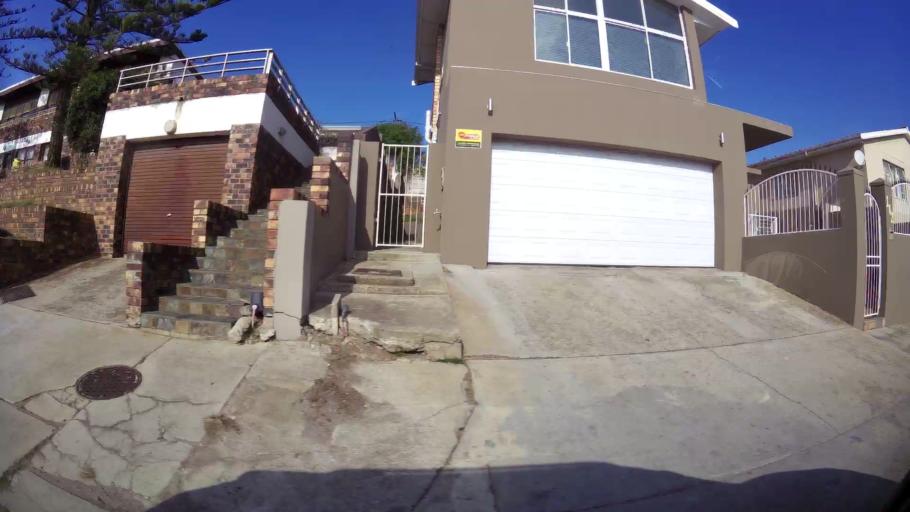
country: ZA
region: Eastern Cape
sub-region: Nelson Mandela Bay Metropolitan Municipality
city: Port Elizabeth
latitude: -33.9270
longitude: 25.5421
